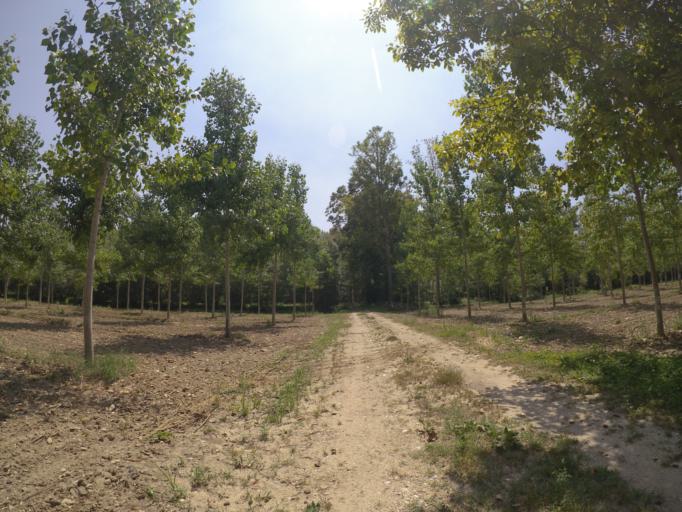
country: IT
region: Friuli Venezia Giulia
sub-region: Provincia di Udine
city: Bertiolo
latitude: 45.9126
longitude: 13.0399
